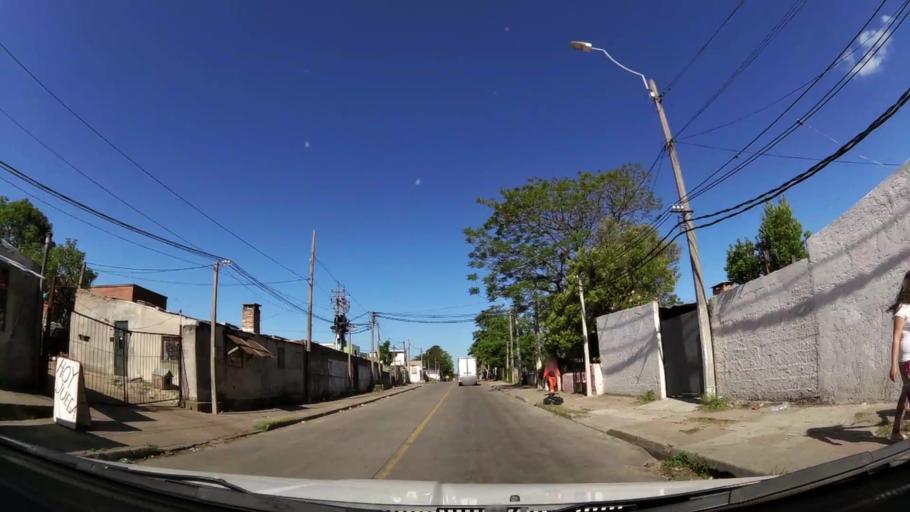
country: UY
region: Montevideo
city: Montevideo
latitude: -34.8351
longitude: -56.1641
